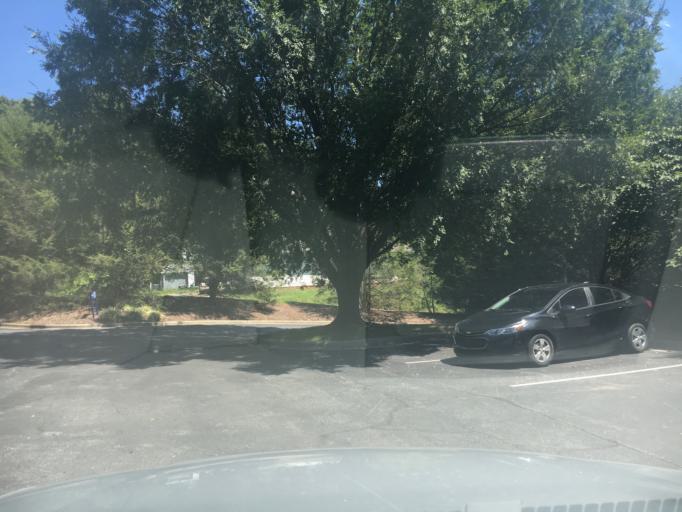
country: US
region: North Carolina
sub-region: McDowell County
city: Marion
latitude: 35.6789
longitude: -82.0225
